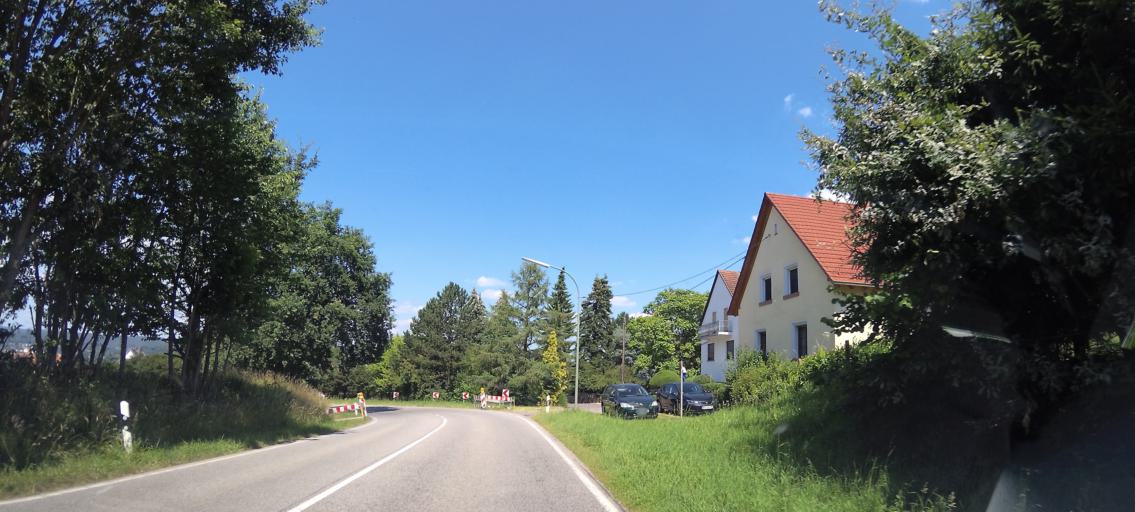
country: DE
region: Saarland
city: Merzig
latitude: 49.4370
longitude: 6.6162
